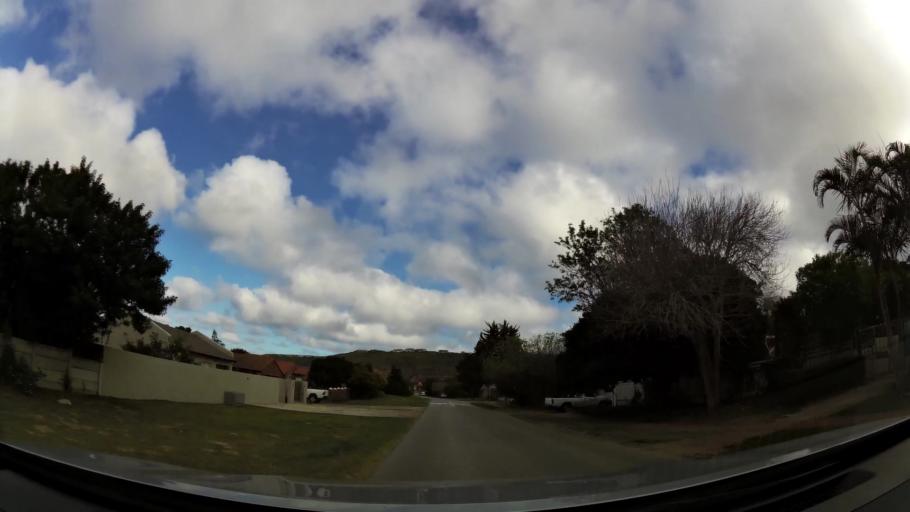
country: ZA
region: Western Cape
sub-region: Eden District Municipality
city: Plettenberg Bay
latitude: -34.0807
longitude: 23.3634
